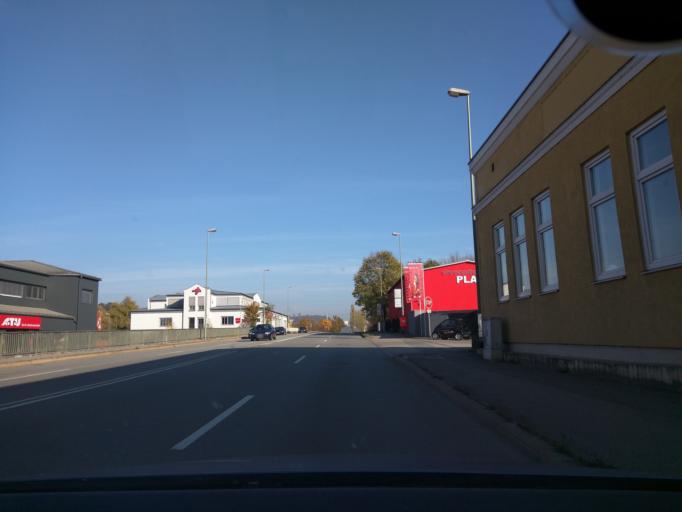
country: DE
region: Bavaria
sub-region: Lower Bavaria
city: Passau
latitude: 48.5734
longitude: 13.4234
